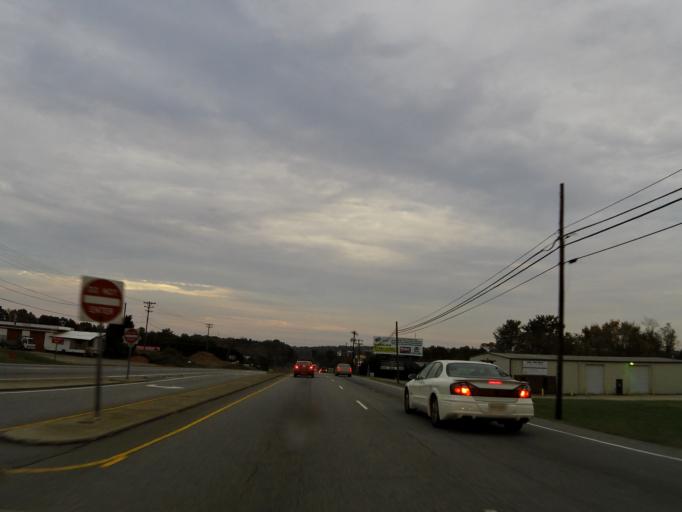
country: US
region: North Carolina
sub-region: Caldwell County
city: Northlakes
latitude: 35.7676
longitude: -81.3867
